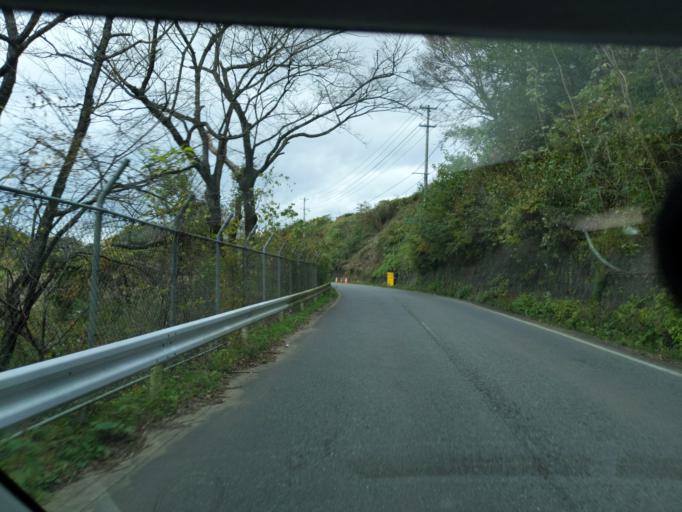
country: JP
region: Iwate
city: Mizusawa
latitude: 39.0509
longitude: 141.1131
